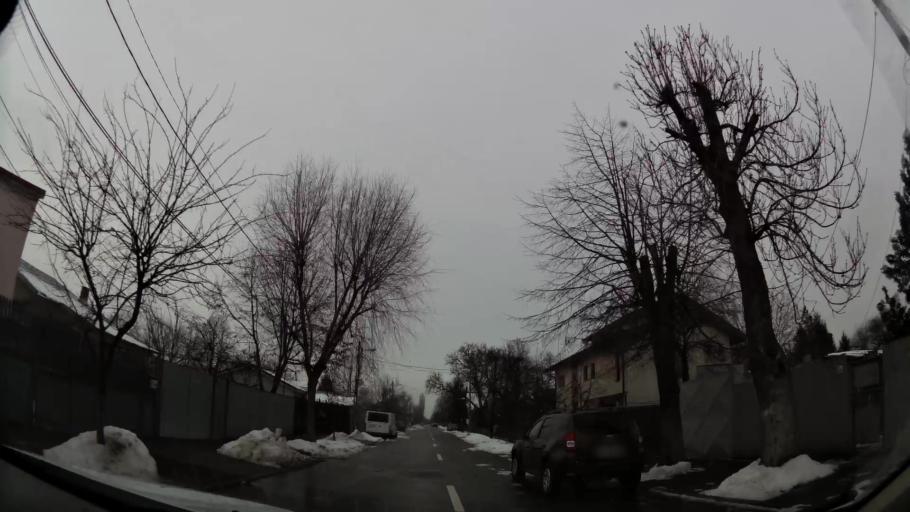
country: RO
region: Ilfov
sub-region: Comuna Mogosoaia
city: Mogosoaia
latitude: 44.5107
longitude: 26.0251
